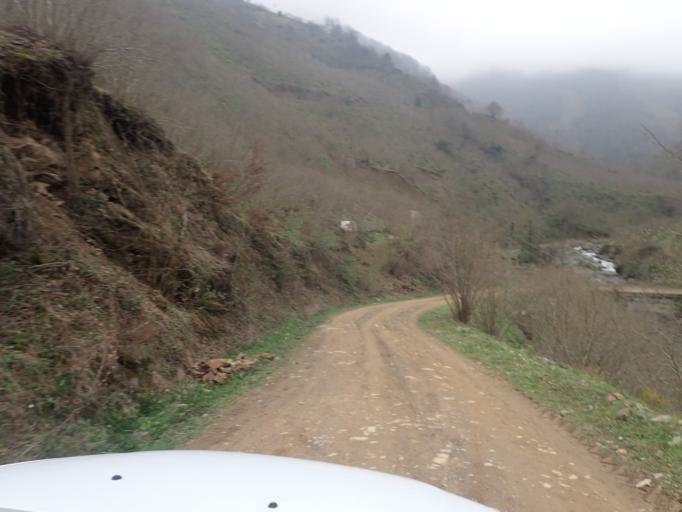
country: TR
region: Ordu
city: Camas
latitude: 40.9010
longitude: 37.5536
